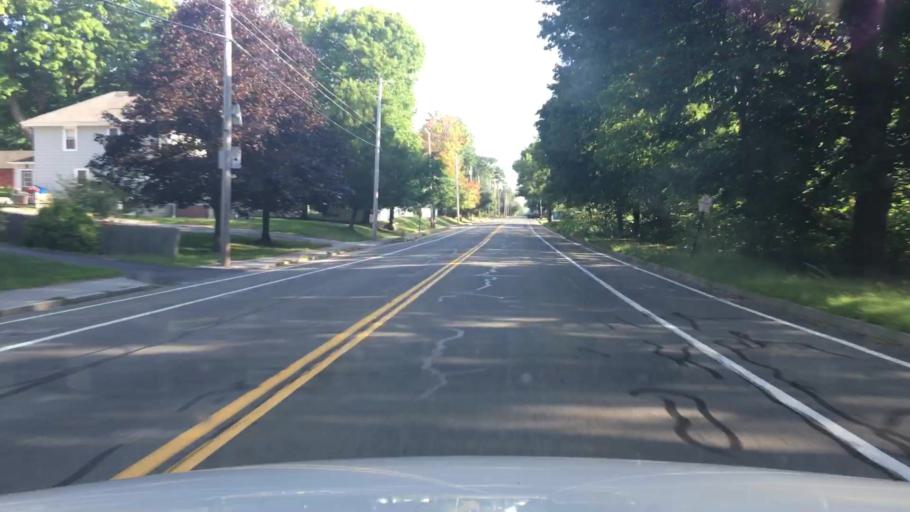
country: US
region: Maine
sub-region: Cumberland County
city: Falmouth
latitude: 43.7175
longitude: -70.2929
